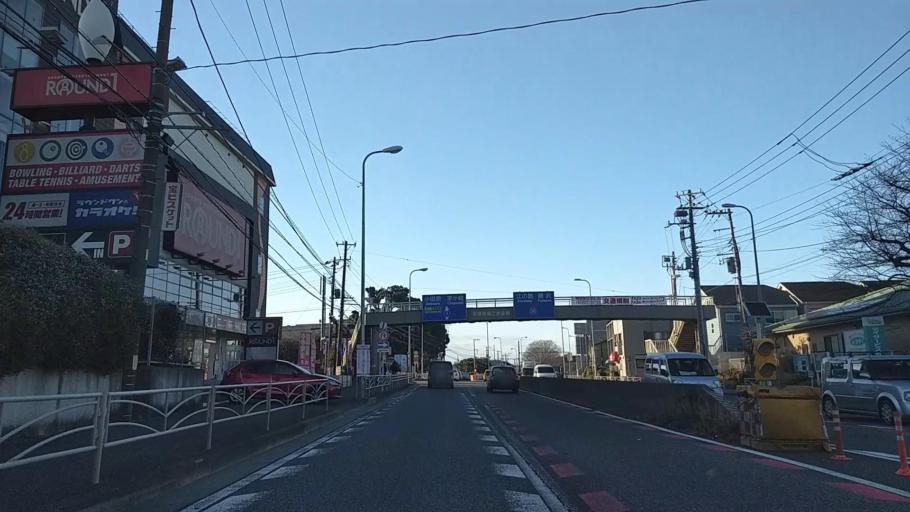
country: JP
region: Kanagawa
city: Fujisawa
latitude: 35.3647
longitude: 139.4977
